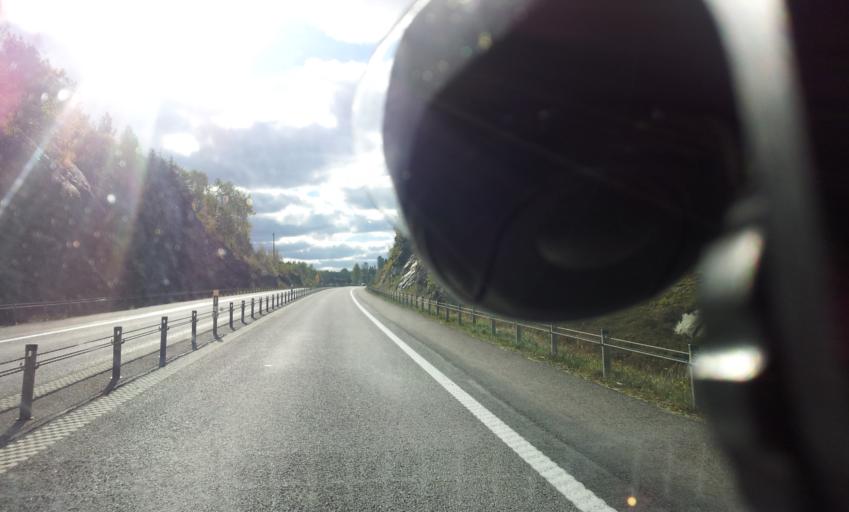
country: SE
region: OEstergoetland
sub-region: Valdemarsviks Kommun
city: Gusum
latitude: 58.2731
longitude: 16.5168
